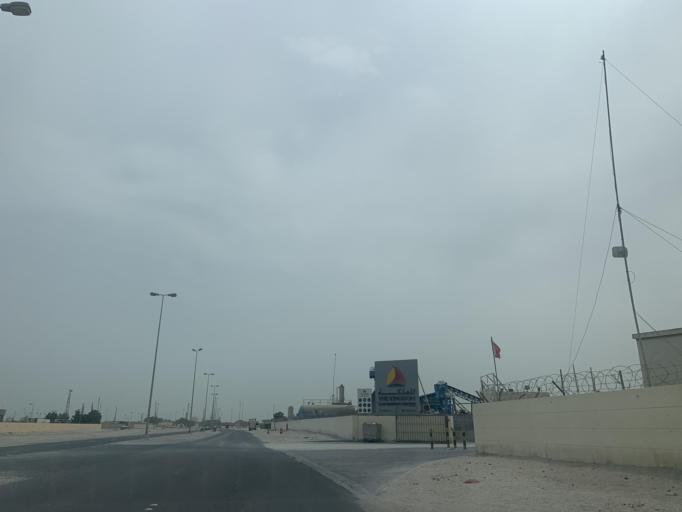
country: BH
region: Muharraq
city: Al Hadd
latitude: 26.2060
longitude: 50.6596
